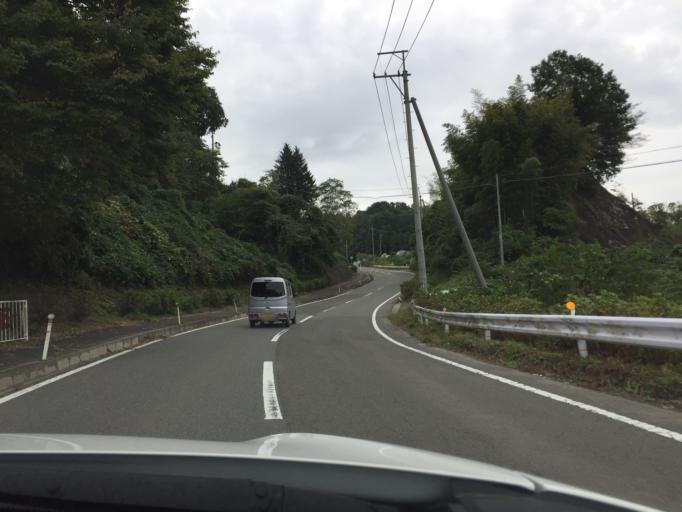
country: JP
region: Fukushima
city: Nihommatsu
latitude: 37.5844
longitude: 140.5574
